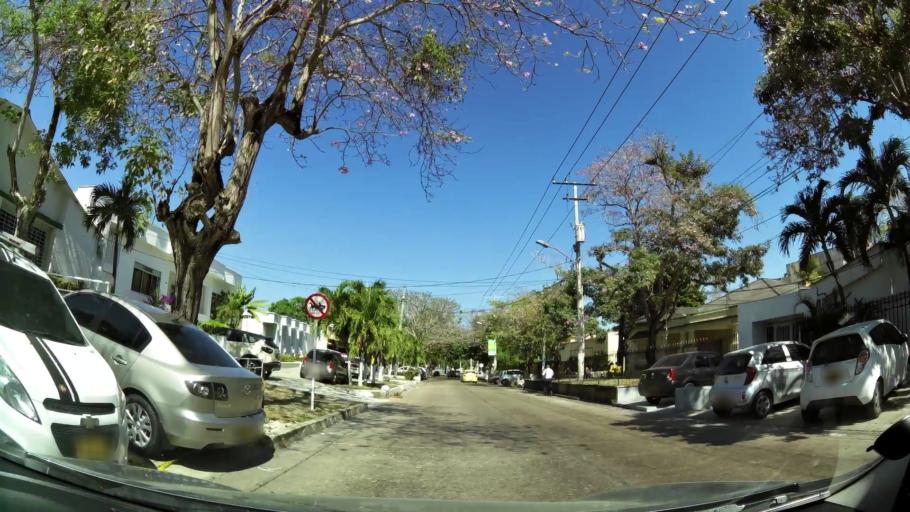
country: CO
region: Atlantico
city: Barranquilla
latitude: 10.9961
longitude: -74.7943
